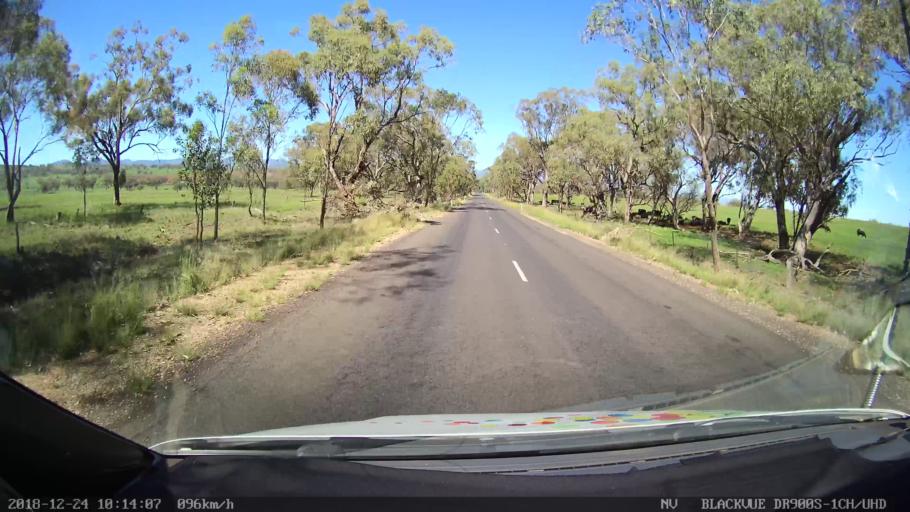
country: AU
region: New South Wales
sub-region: Liverpool Plains
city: Quirindi
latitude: -31.6953
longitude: 150.6325
